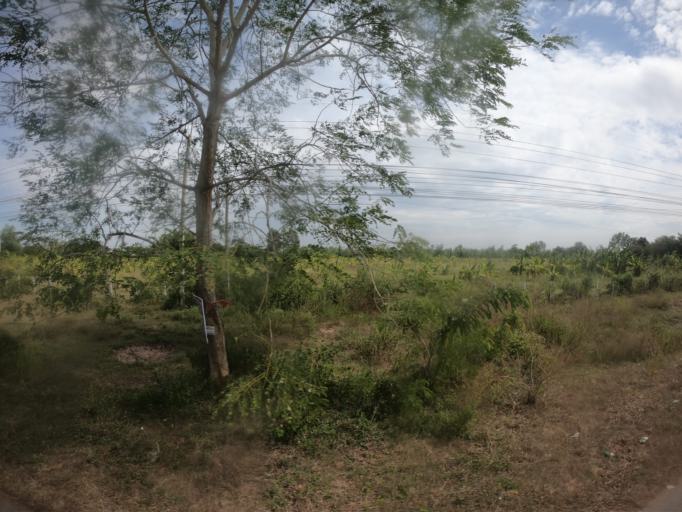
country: TH
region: Maha Sarakham
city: Chiang Yuen
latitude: 16.3644
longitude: 103.1077
